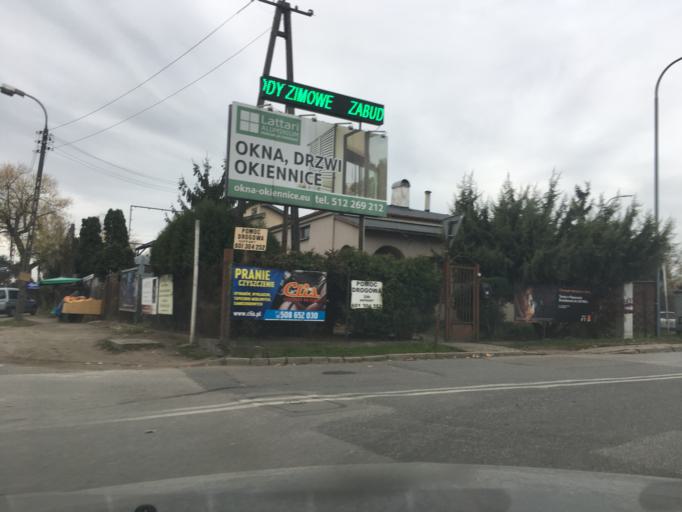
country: PL
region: Masovian Voivodeship
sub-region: Powiat piaseczynski
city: Piaseczno
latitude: 52.0564
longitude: 21.0080
